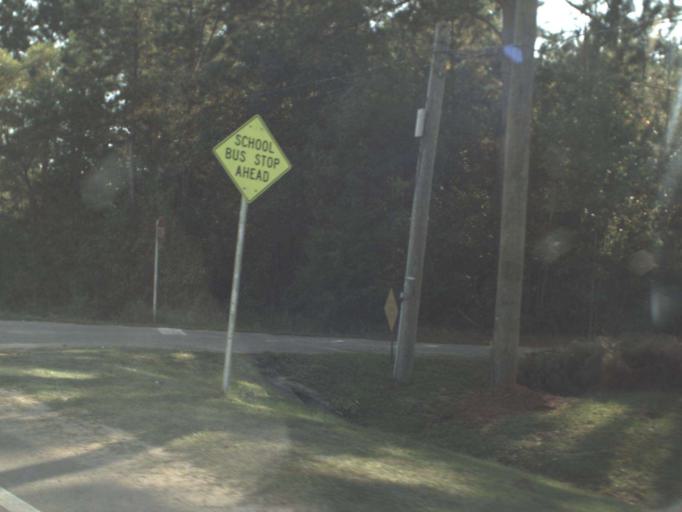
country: US
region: Florida
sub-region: Holmes County
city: Bonifay
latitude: 30.6095
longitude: -85.7155
